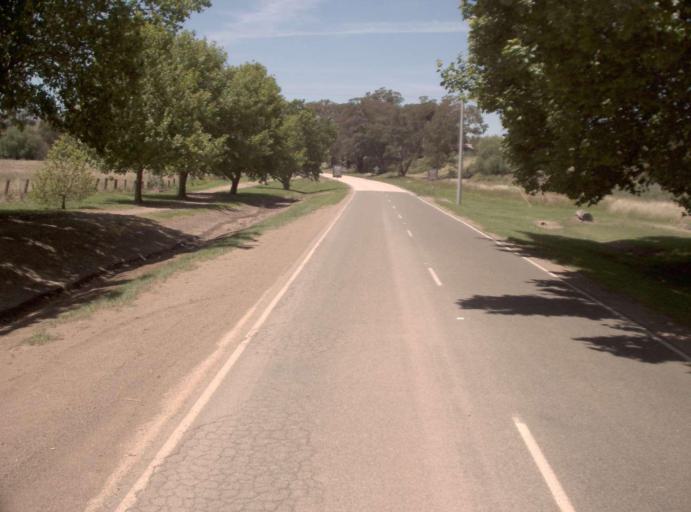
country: AU
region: Victoria
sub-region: East Gippsland
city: Bairnsdale
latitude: -37.2707
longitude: 147.7258
